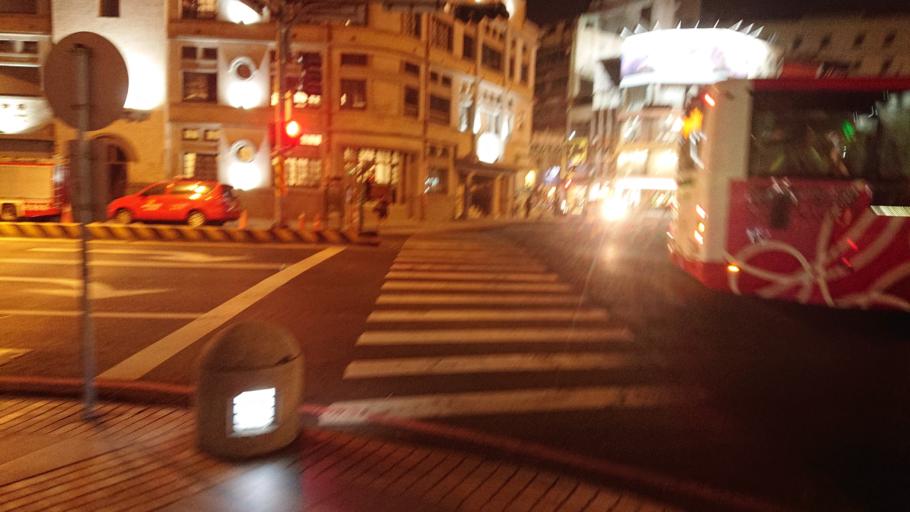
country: TW
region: Taiwan
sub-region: Tainan
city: Tainan
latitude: 22.9923
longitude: 120.2046
